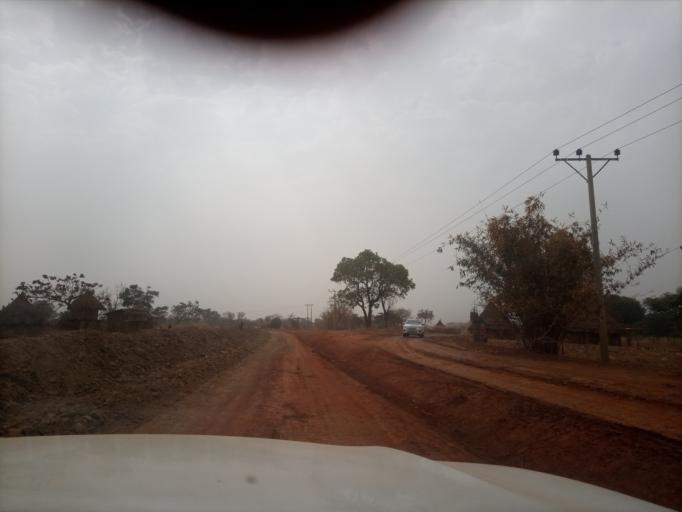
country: ET
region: Oromiya
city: Mendi
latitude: 10.1299
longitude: 35.1293
